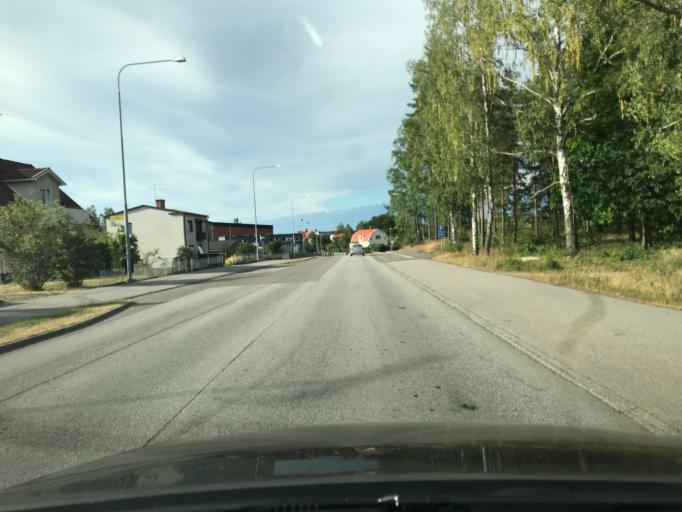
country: SE
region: Kalmar
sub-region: Hultsfreds Kommun
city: Hultsfred
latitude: 57.4820
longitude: 15.8419
